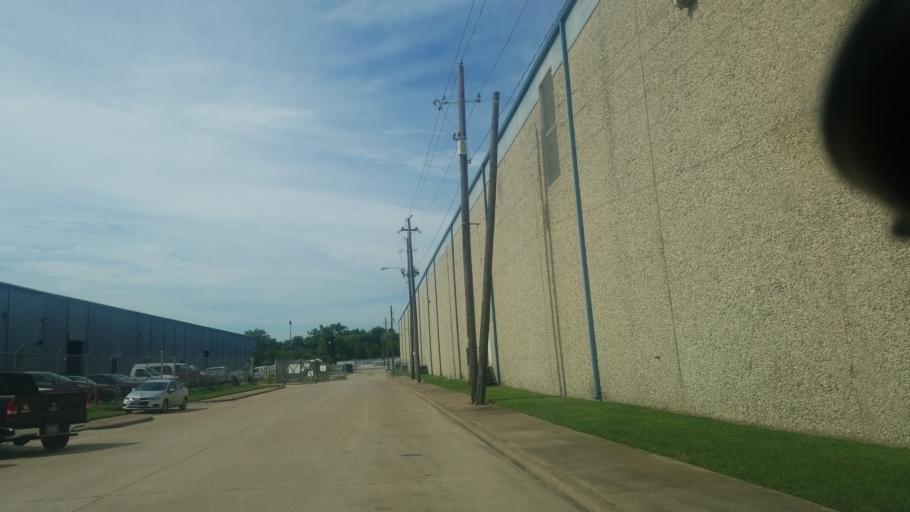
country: US
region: Texas
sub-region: Dallas County
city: Dallas
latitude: 32.7775
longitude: -96.8529
